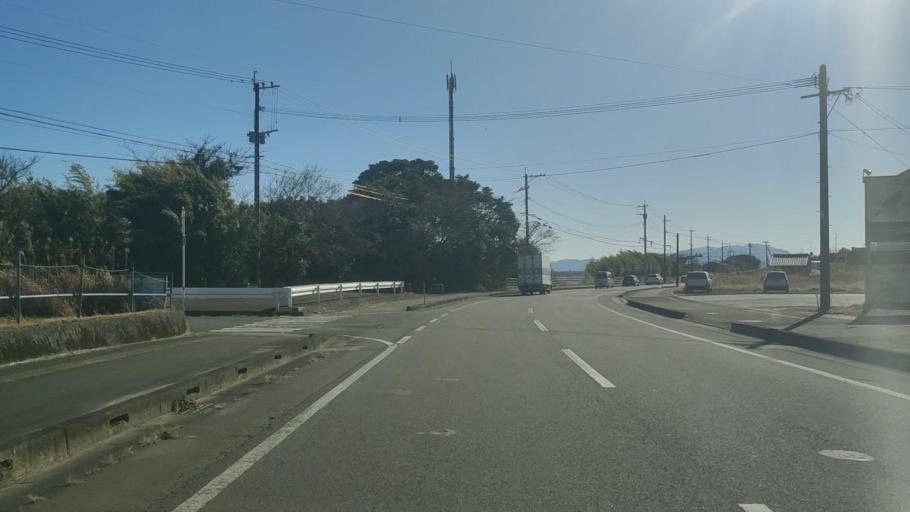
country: JP
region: Miyazaki
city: Miyazaki-shi
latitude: 31.9491
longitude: 131.4601
